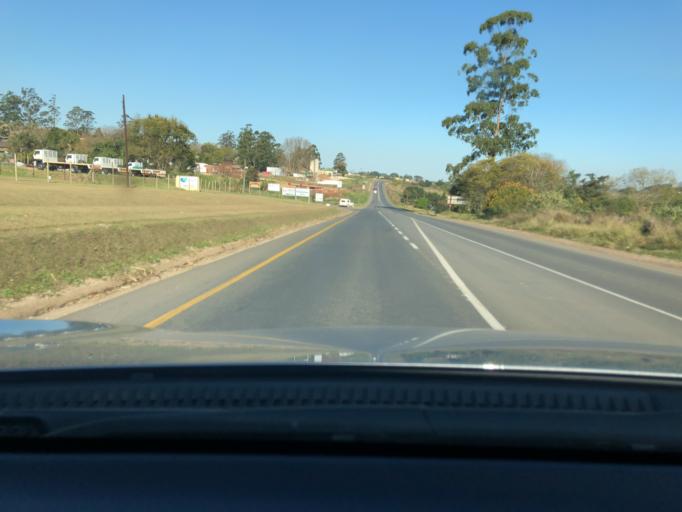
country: ZA
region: KwaZulu-Natal
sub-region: uMgungundlovu District Municipality
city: Camperdown
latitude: -29.7293
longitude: 30.5022
